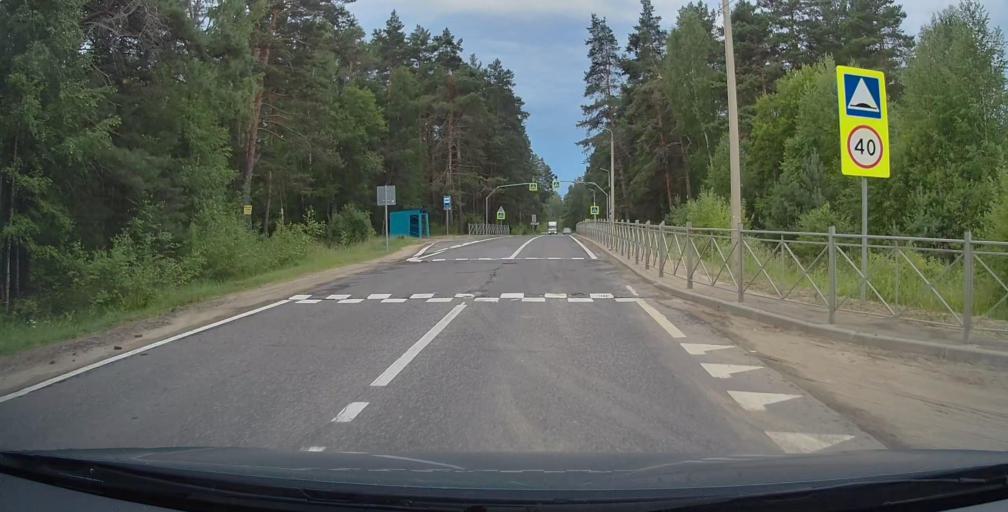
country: RU
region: Jaroslavl
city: Myshkin
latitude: 57.7975
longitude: 38.5005
